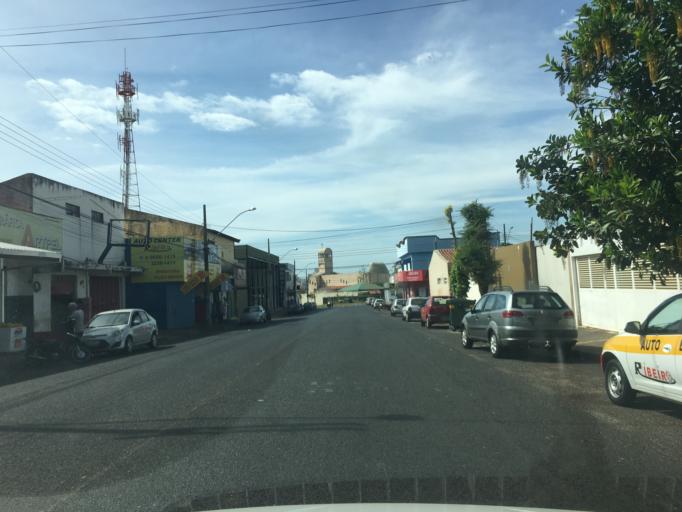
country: BR
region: Minas Gerais
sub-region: Uberlandia
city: Uberlandia
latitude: -18.9380
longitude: -48.3013
